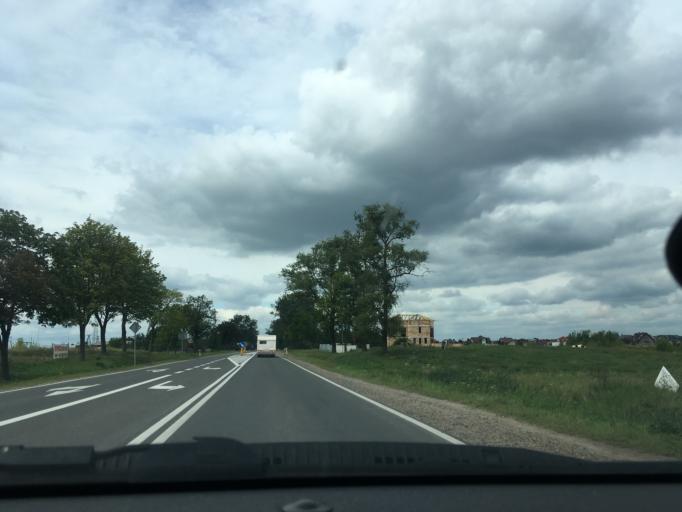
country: PL
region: Podlasie
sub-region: Powiat augustowski
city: Augustow
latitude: 53.8396
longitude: 22.9665
